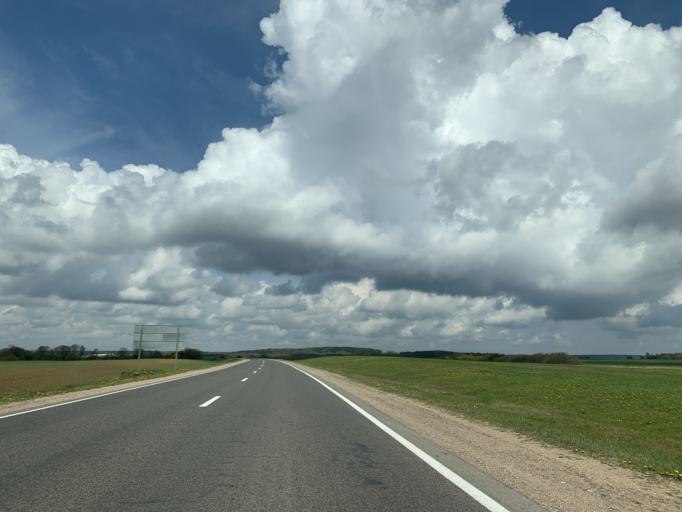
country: BY
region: Minsk
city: Nyasvizh
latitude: 53.2314
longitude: 26.7224
